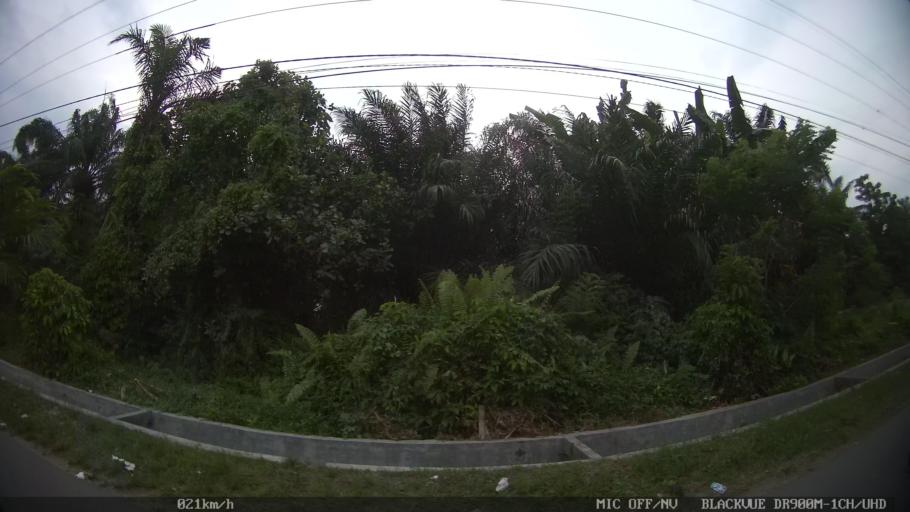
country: ID
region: North Sumatra
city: Sunggal
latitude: 3.5697
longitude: 98.6044
